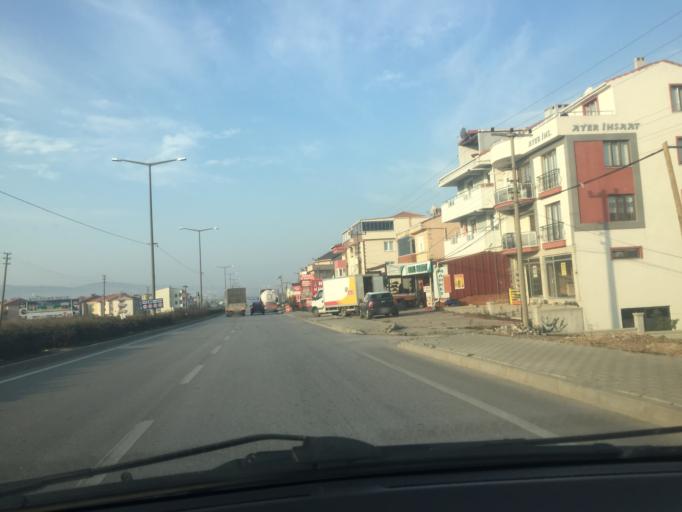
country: TR
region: Canakkale
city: Biga
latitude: 40.2440
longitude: 27.2722
